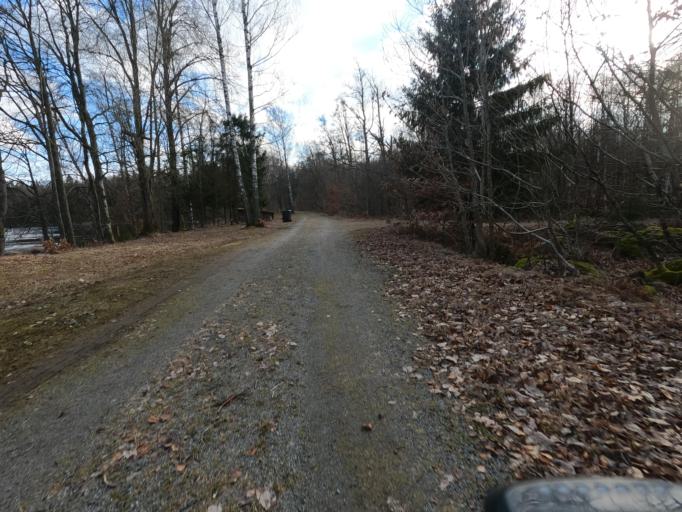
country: SE
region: Kronoberg
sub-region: Vaxjo Kommun
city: Gemla
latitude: 56.6609
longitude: 14.6199
